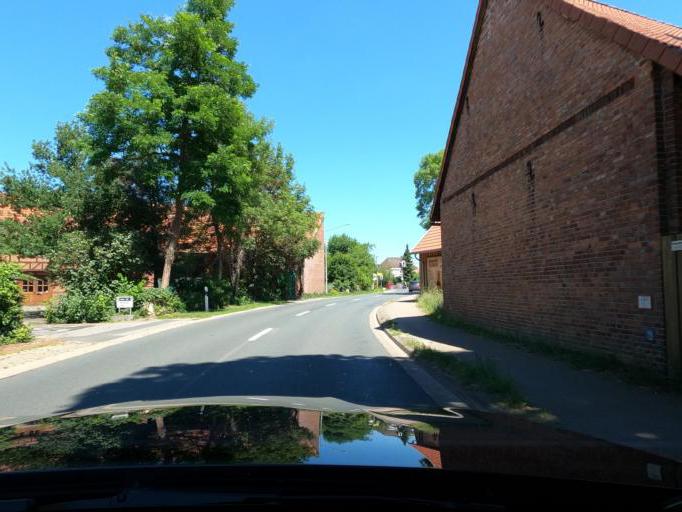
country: DE
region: Lower Saxony
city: Burgdorf
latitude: 52.4154
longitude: 9.9777
